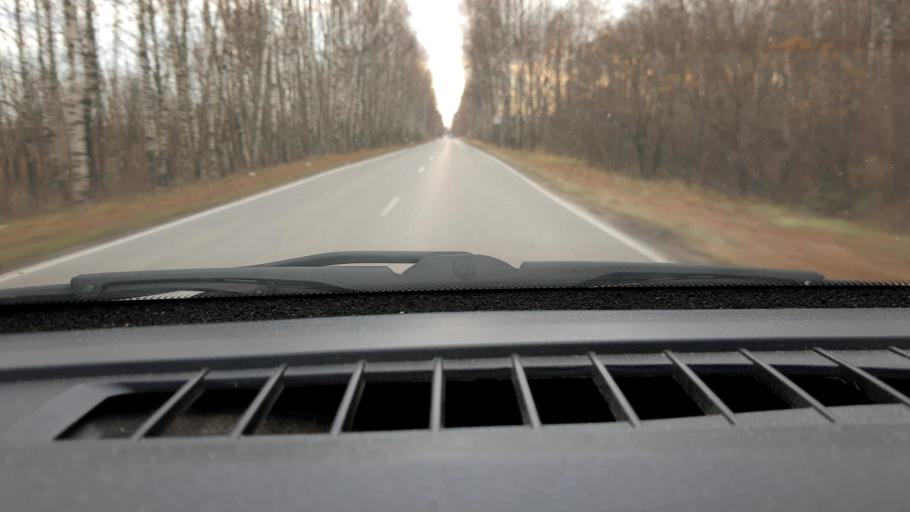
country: RU
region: Nizjnij Novgorod
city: Neklyudovo
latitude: 56.5126
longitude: 43.8396
